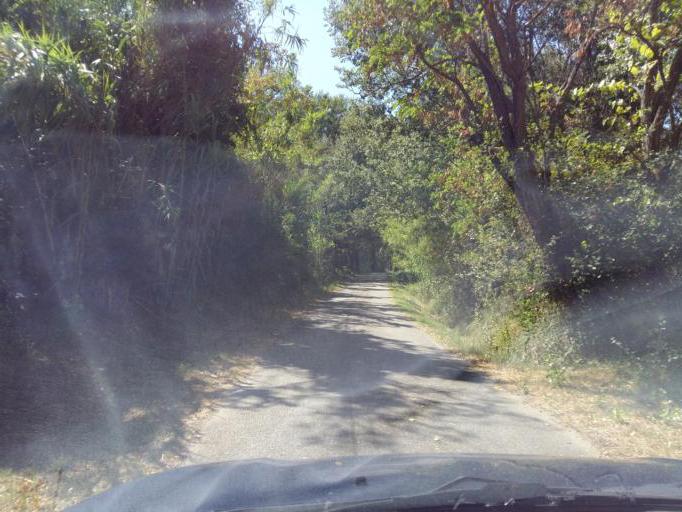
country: FR
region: Provence-Alpes-Cote d'Azur
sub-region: Departement du Vaucluse
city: Loriol-du-Comtat
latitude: 44.0881
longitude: 5.0112
